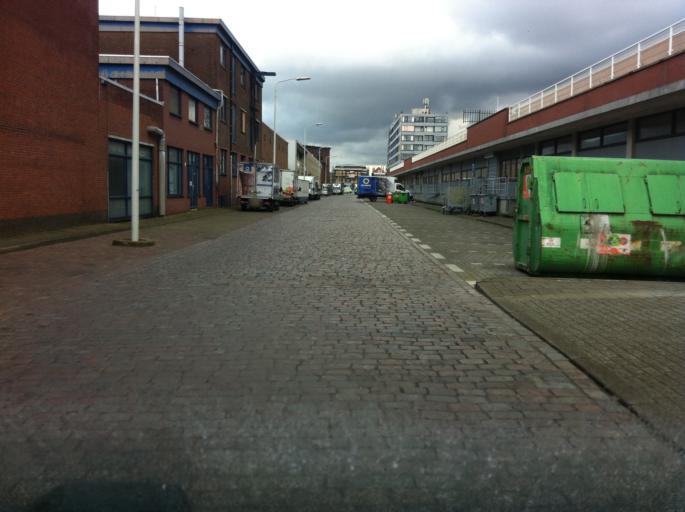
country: NL
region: South Holland
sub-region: Gemeente Den Haag
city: Scheveningen
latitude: 52.0995
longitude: 4.2688
